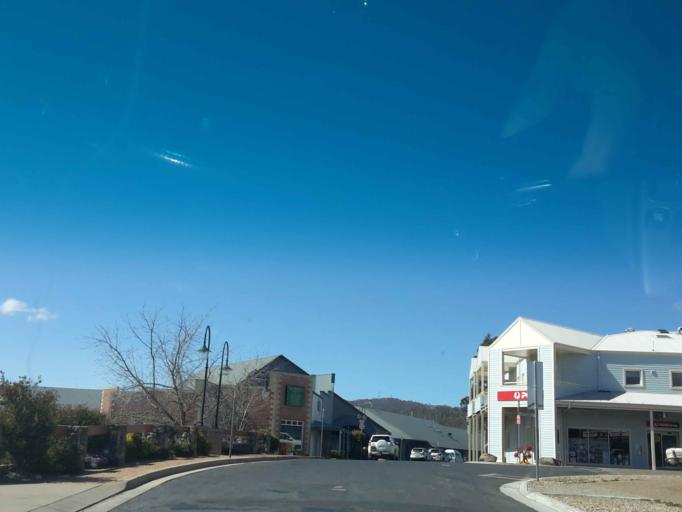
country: AU
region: New South Wales
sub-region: Snowy River
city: Jindabyne
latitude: -36.4154
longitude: 148.6207
